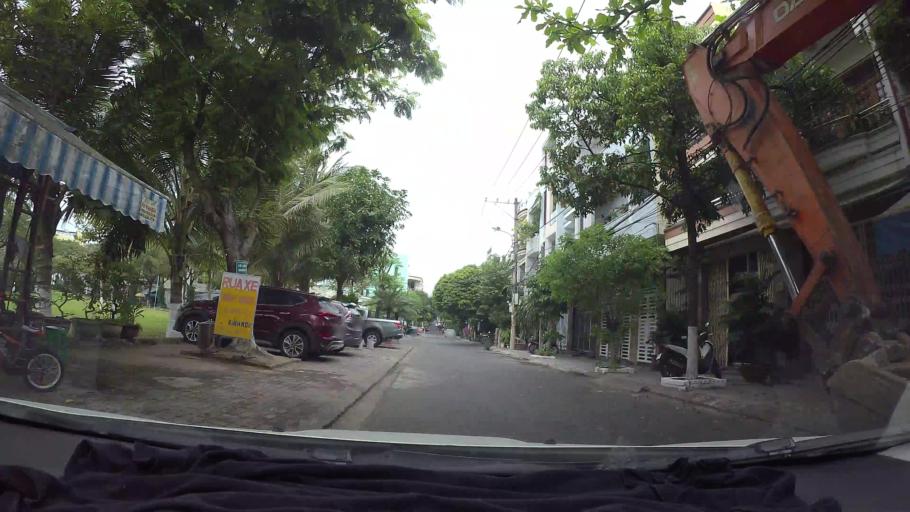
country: VN
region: Da Nang
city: Da Nang
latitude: 16.0874
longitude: 108.2193
